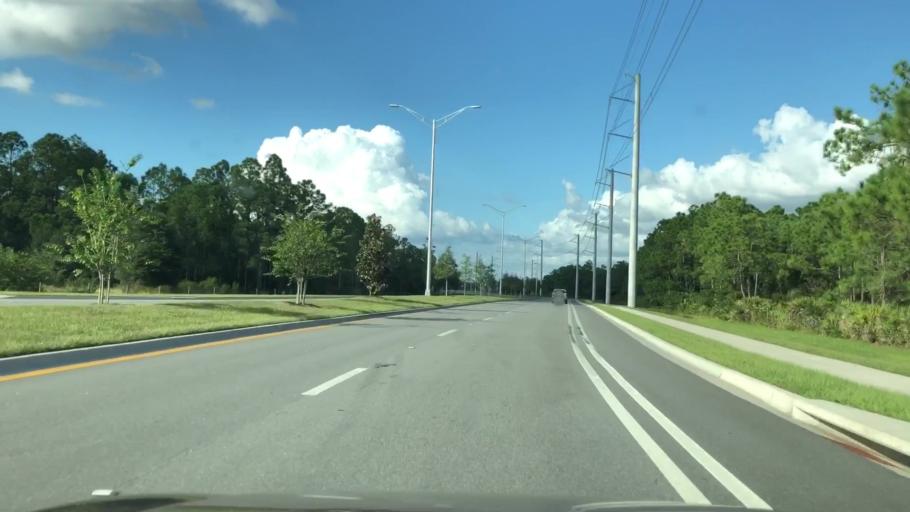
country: US
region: Florida
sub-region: Sarasota County
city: Fruitville
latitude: 27.3547
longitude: -82.3867
